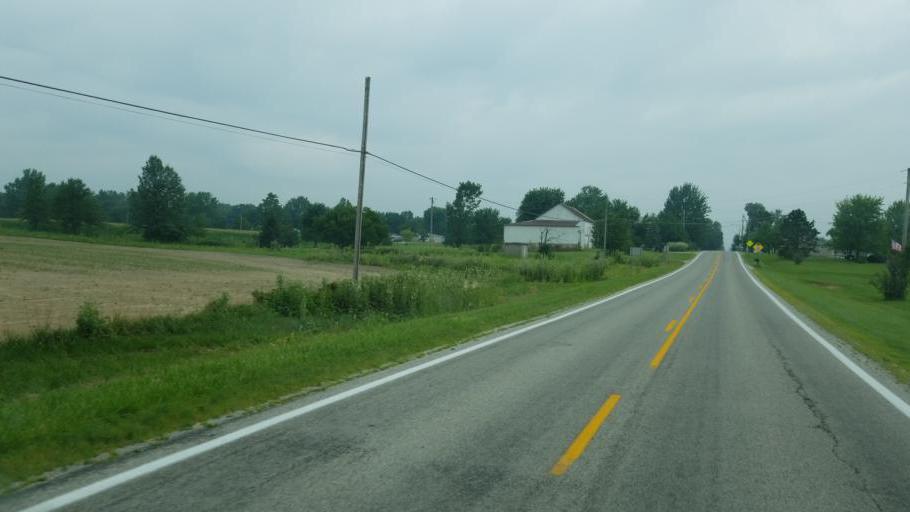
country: US
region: Ohio
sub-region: Union County
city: Richwood
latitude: 40.5802
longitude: -83.3149
